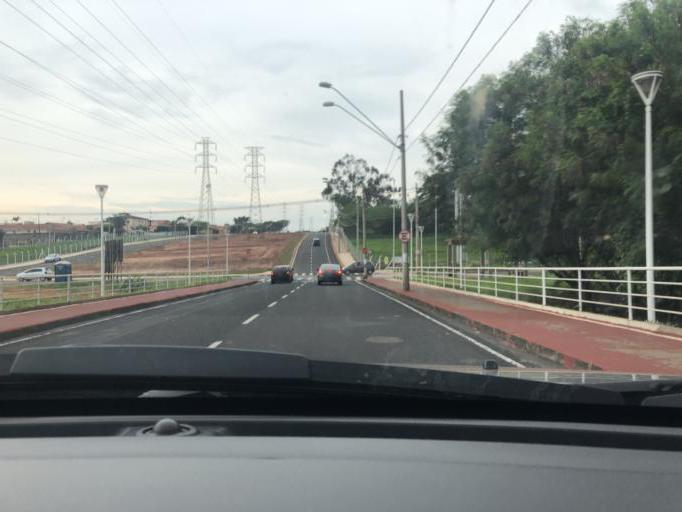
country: BR
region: Sao Paulo
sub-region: Sao Jose Do Rio Preto
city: Sao Jose do Rio Preto
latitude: -20.8432
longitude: -49.4105
